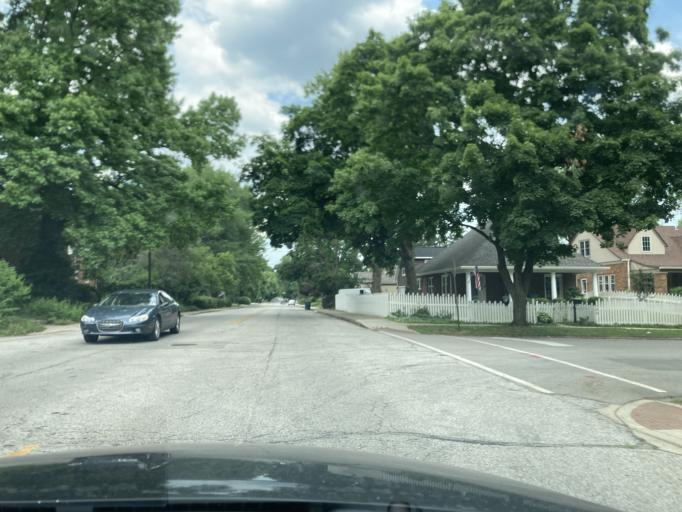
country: US
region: Indiana
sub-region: Marion County
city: Broad Ripple
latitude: 39.8374
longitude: -86.1617
